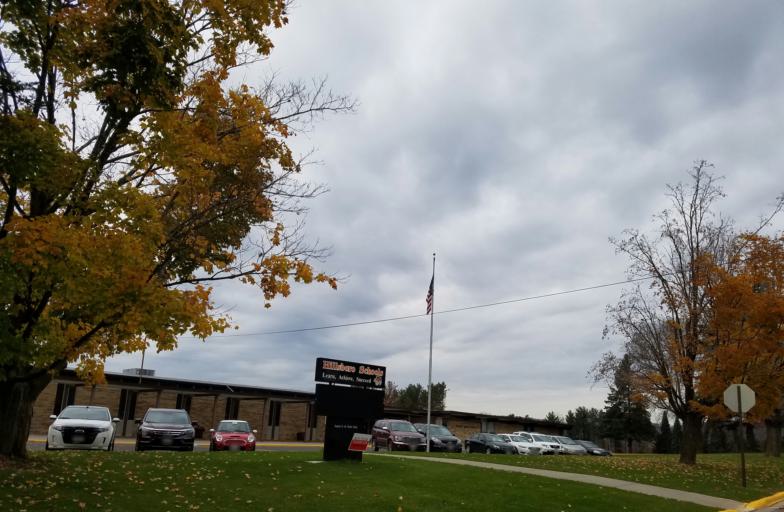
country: US
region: Wisconsin
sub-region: Vernon County
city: Hillsboro
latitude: 43.6563
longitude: -90.3509
